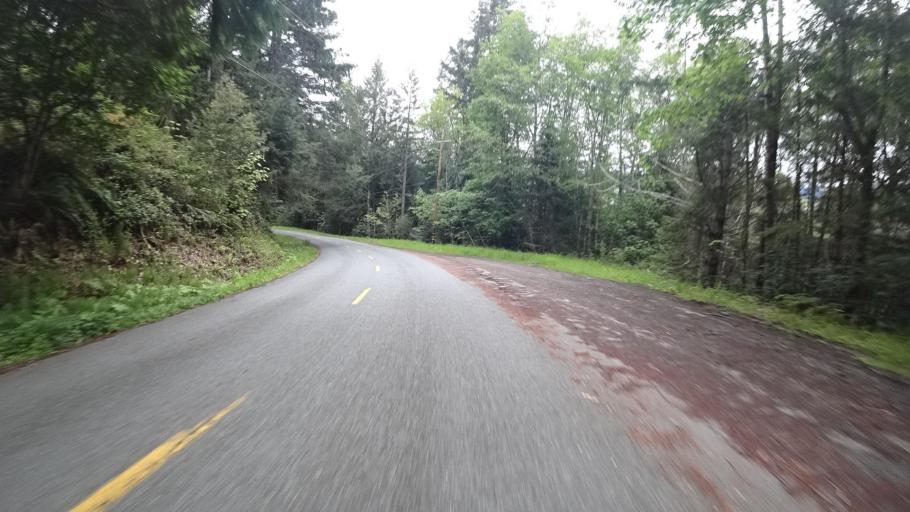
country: US
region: California
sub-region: Humboldt County
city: Blue Lake
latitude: 40.9449
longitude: -123.8424
